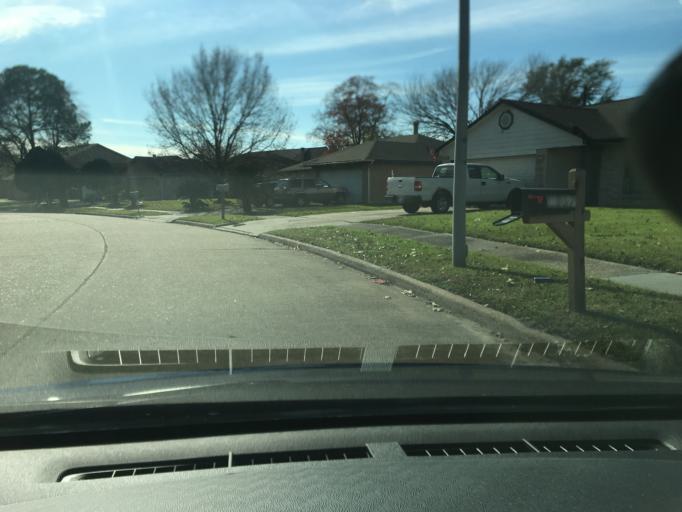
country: US
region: Texas
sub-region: Harris County
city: Cloverleaf
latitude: 29.8079
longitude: -95.1605
